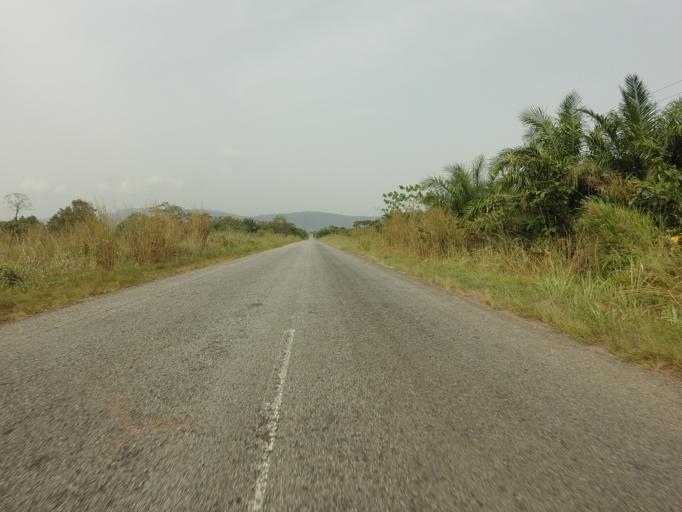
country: GH
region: Volta
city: Ho
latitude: 6.5744
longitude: 0.3405
